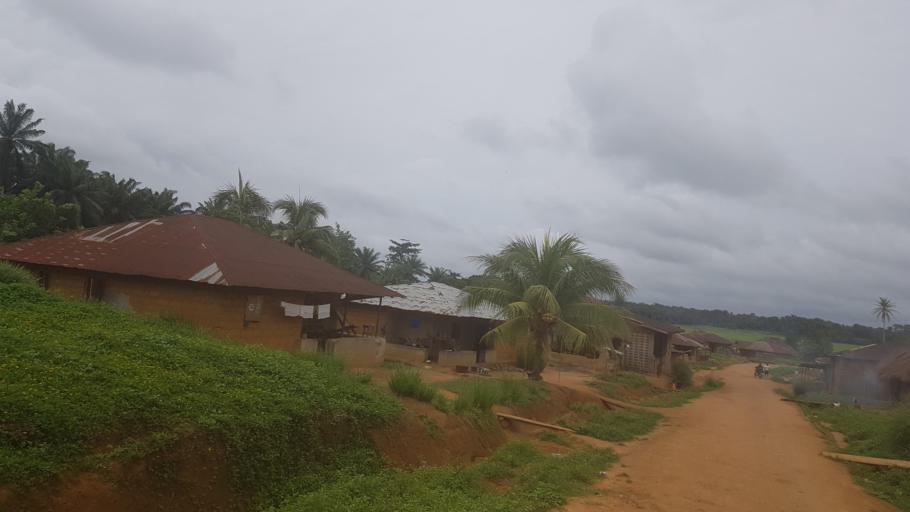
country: SL
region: Southern Province
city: Sumbuya
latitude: 7.5329
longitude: -12.1772
